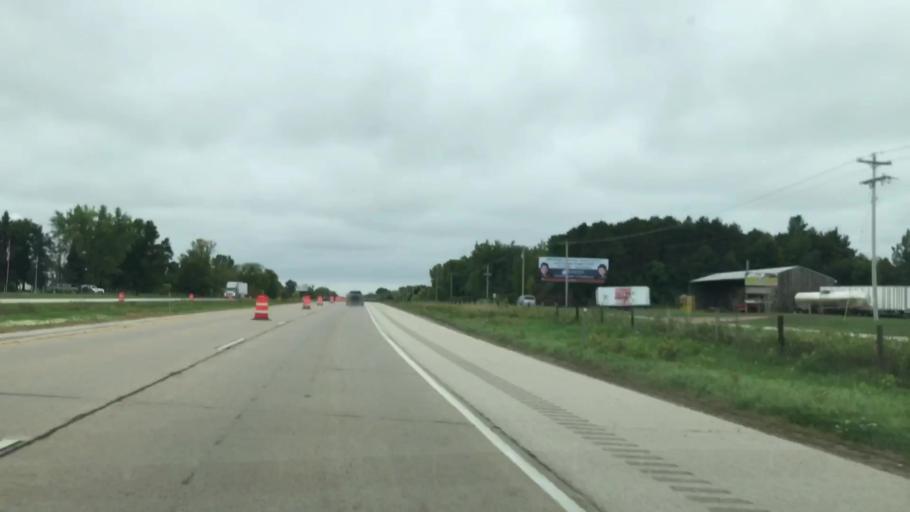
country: US
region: Wisconsin
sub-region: Brown County
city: Suamico
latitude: 44.7354
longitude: -88.0510
